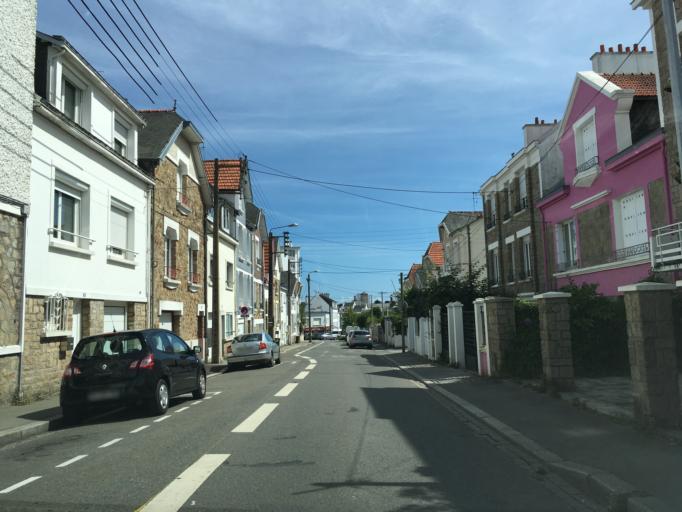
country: FR
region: Brittany
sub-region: Departement du Morbihan
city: Lorient
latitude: 47.7495
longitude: -3.3753
